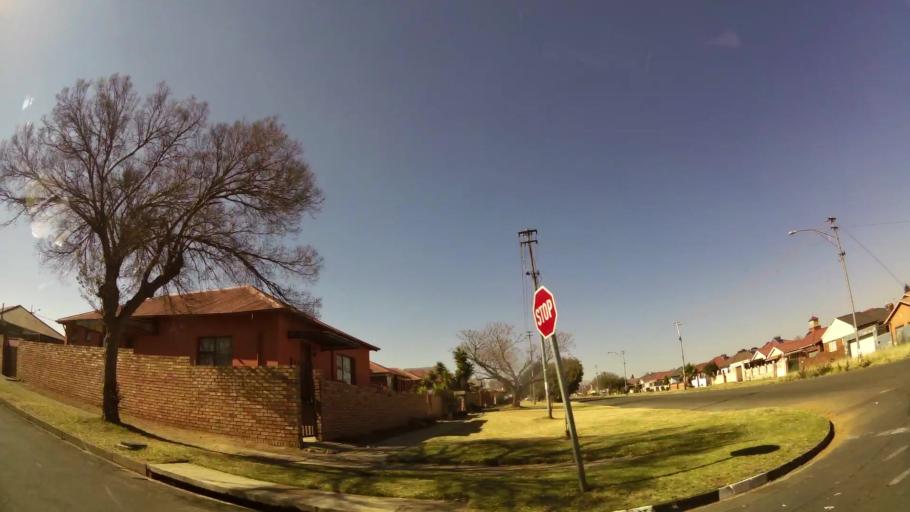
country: ZA
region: Gauteng
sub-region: City of Johannesburg Metropolitan Municipality
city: Johannesburg
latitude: -26.1899
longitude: 27.9733
